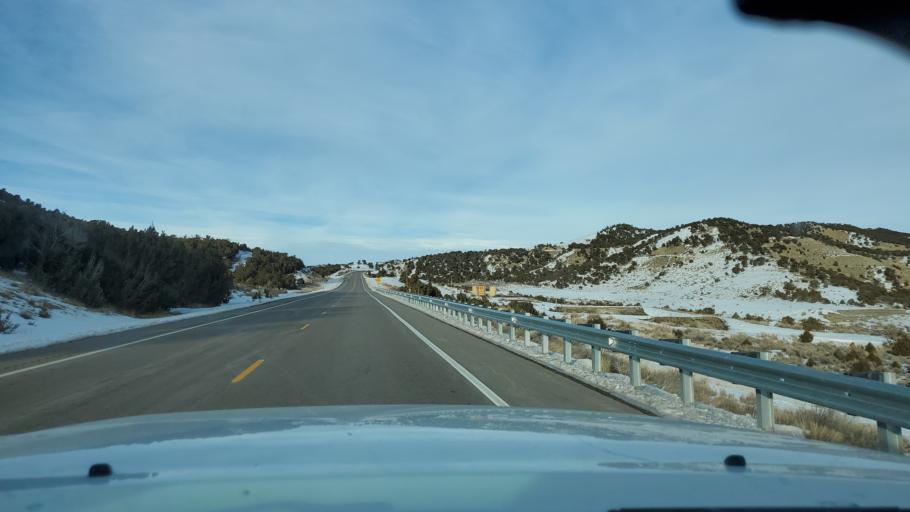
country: US
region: Colorado
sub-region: Rio Blanco County
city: Rangely
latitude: 40.3483
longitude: -108.4540
